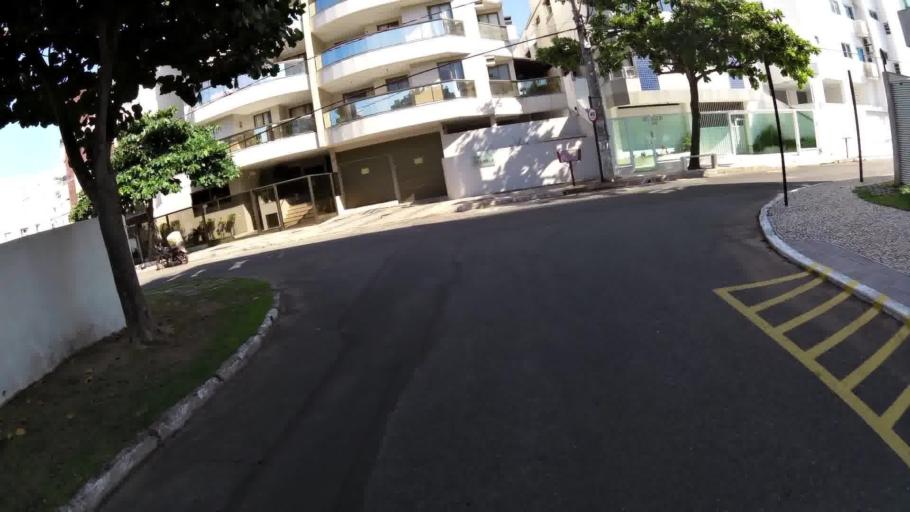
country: BR
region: Espirito Santo
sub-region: Guarapari
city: Guarapari
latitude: -20.7274
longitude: -40.5260
